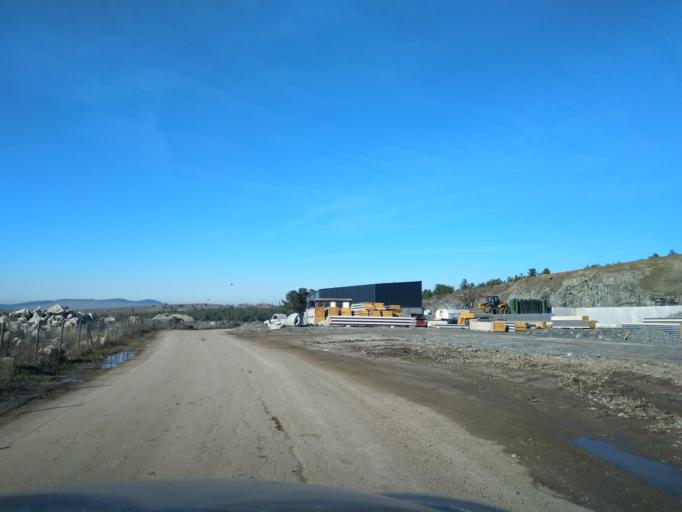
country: RS
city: Zlatibor
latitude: 43.7304
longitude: 19.6819
